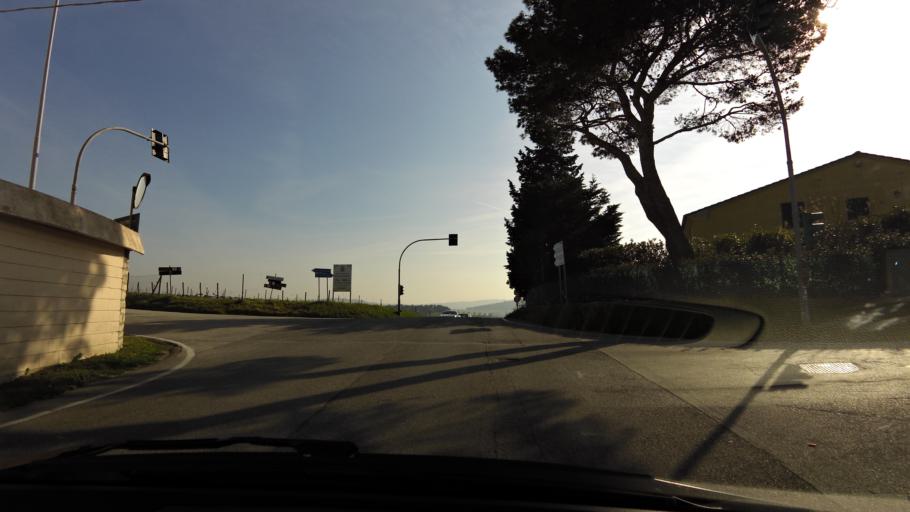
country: IT
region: The Marches
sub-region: Provincia di Ancona
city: Marcelli
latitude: 43.4923
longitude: 13.6148
